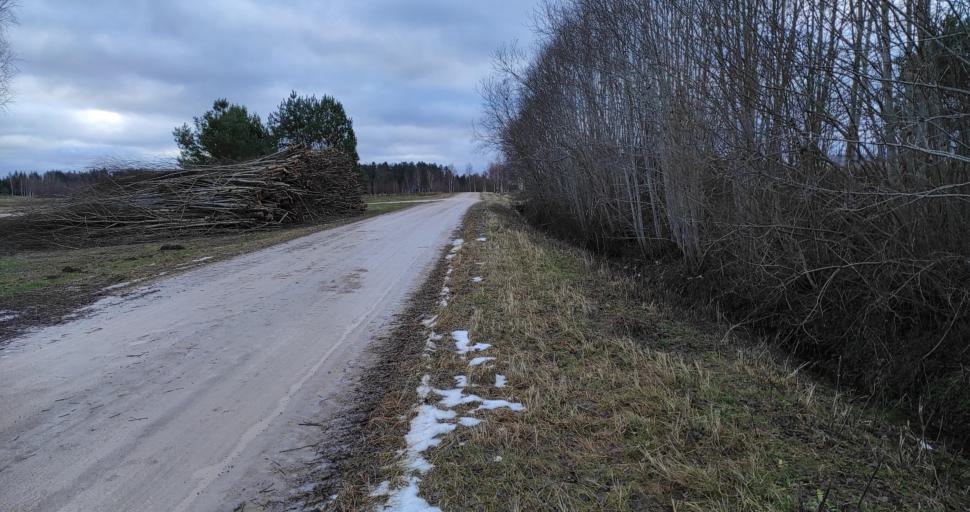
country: LV
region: Talsu Rajons
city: Stende
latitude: 57.0638
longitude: 22.2891
